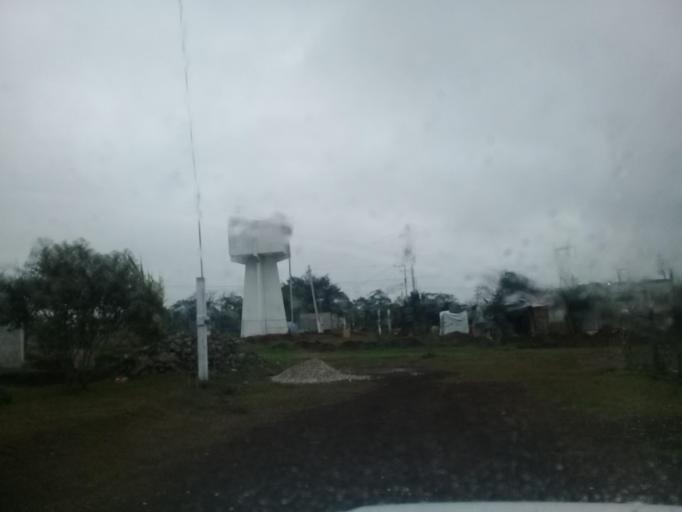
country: MX
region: Veracruz
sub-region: Cordoba
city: Veinte de Noviembre
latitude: 18.8578
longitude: -96.9580
